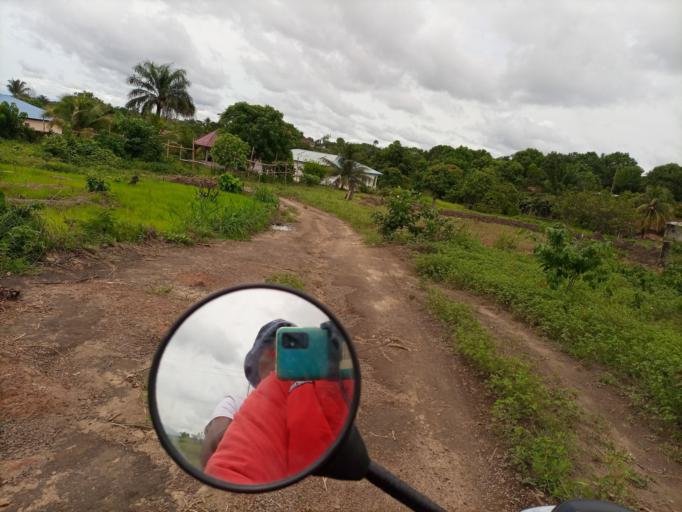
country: SL
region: Southern Province
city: Bo
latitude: 7.9422
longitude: -11.7465
